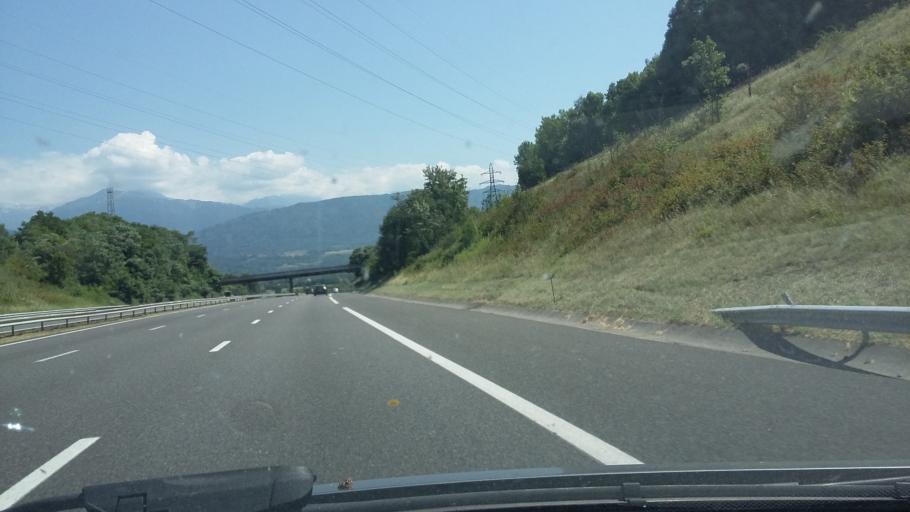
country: FR
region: Rhone-Alpes
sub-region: Departement de la Savoie
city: Les Marches
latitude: 45.5017
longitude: 6.0178
